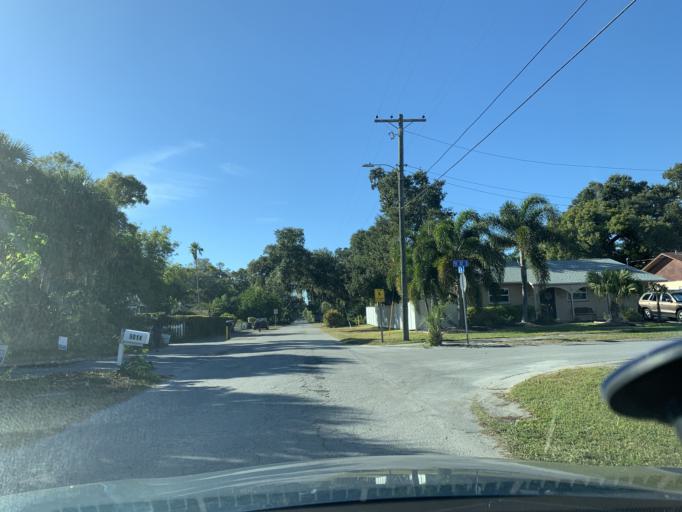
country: US
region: Florida
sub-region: Pinellas County
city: Gulfport
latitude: 27.7447
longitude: -82.7011
